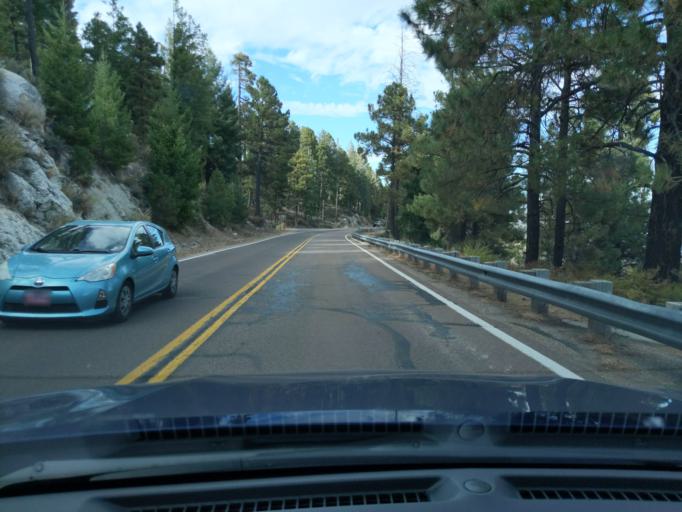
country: US
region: Arizona
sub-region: Pinal County
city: Oracle
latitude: 32.4429
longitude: -110.7533
